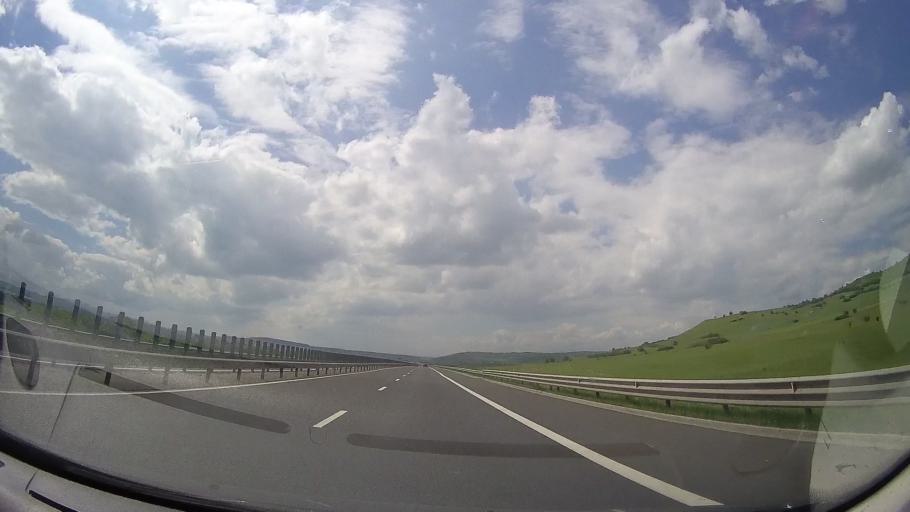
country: RO
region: Sibiu
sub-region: Oras Miercurea Sibiului
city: Miercurea Sibiului
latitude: 45.8943
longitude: 23.8163
